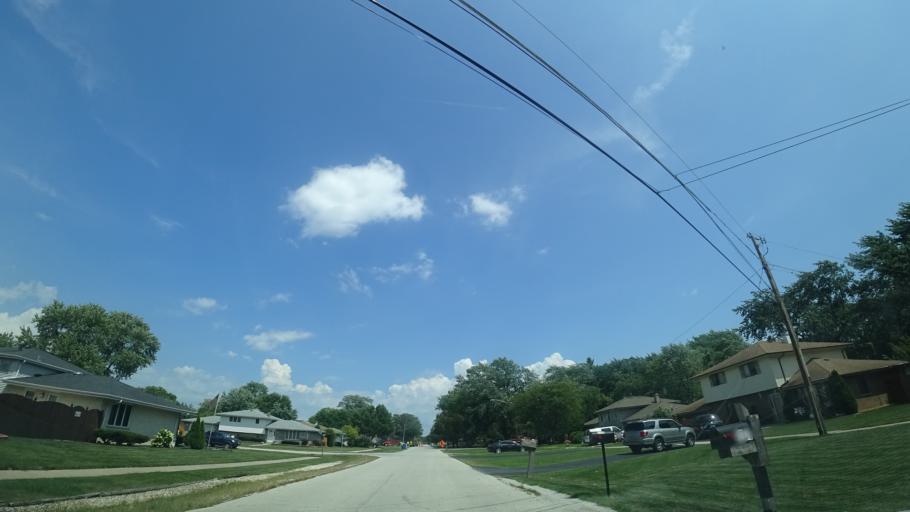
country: US
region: Illinois
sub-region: Cook County
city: Alsip
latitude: 41.6762
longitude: -87.7483
